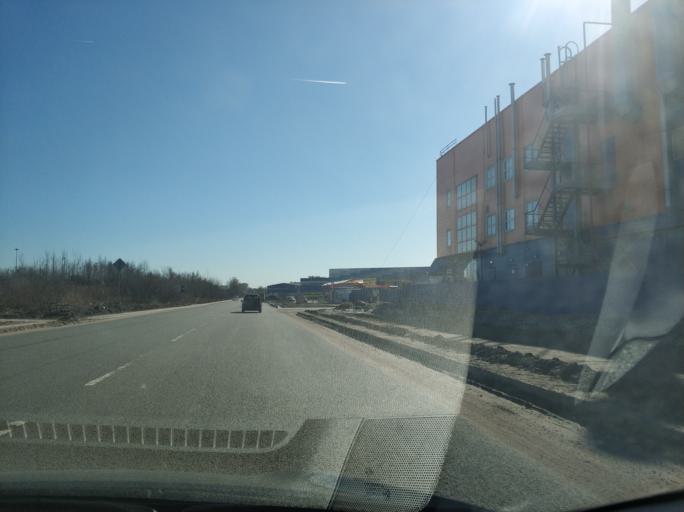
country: RU
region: Leningrad
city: Bugry
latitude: 60.0678
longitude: 30.3818
